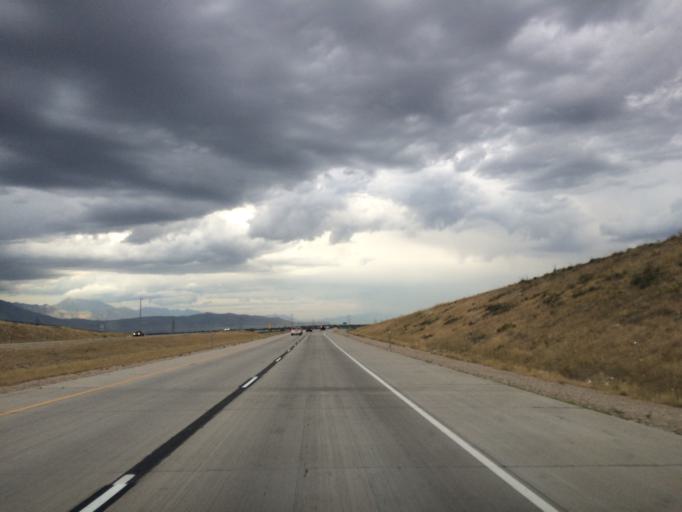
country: US
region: Utah
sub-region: Salt Lake County
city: Oquirrh
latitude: 40.6155
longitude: -112.0400
